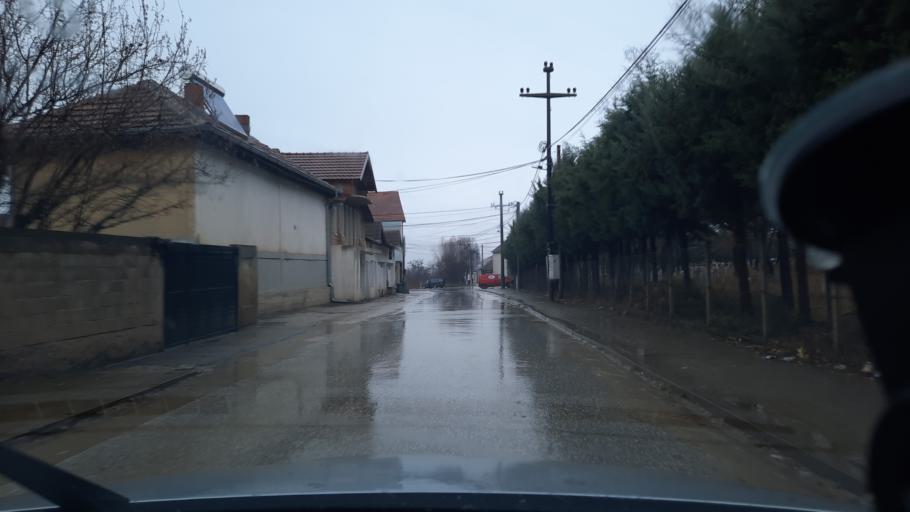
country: MK
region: Opstina Lipkovo
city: Lipkovo
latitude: 42.1521
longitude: 21.5918
